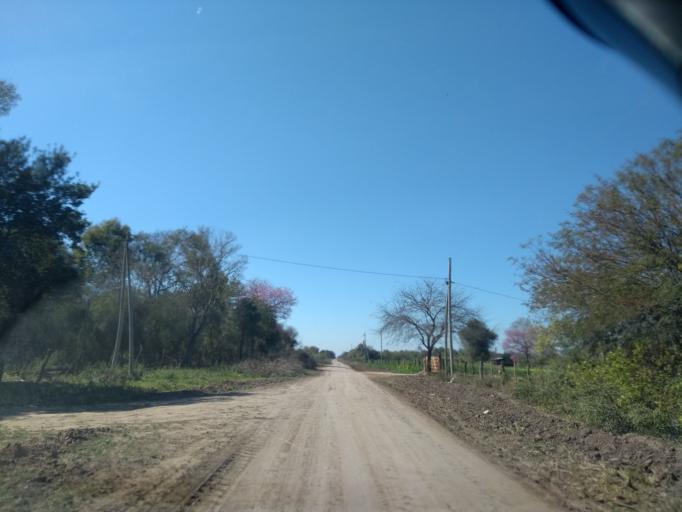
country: AR
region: Chaco
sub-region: Departamento de Quitilipi
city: Quitilipi
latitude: -26.7454
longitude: -60.2761
